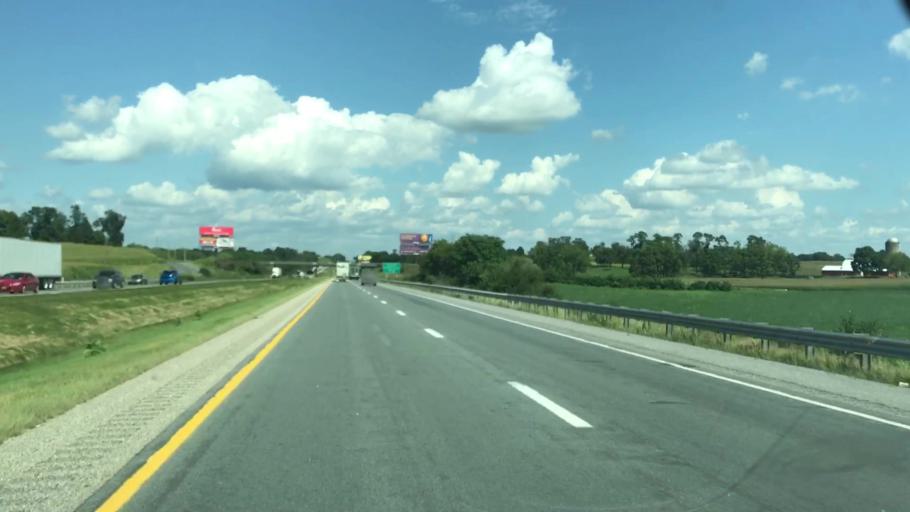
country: US
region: Pennsylvania
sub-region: Cumberland County
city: Newville
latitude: 40.1139
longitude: -77.3744
